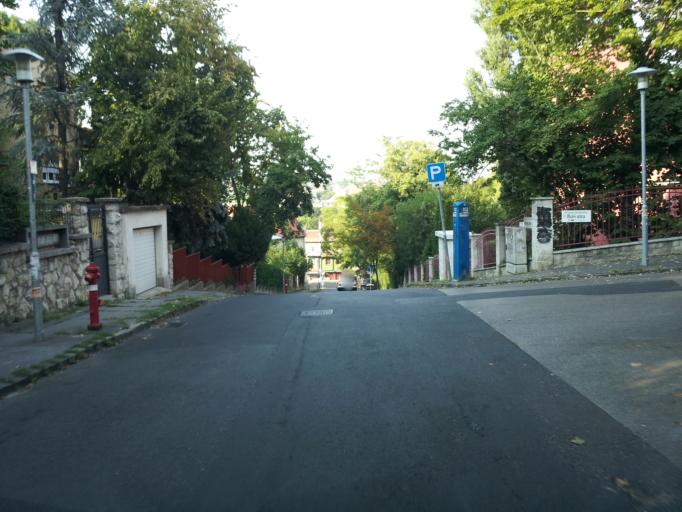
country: HU
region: Budapest
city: Budapest XII. keruelet
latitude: 47.5056
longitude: 19.0147
